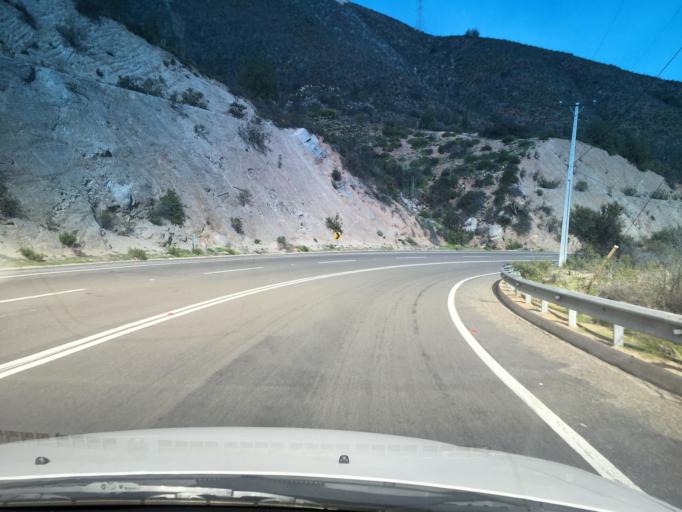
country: CL
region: Valparaiso
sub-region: Provincia de San Felipe
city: Llaillay
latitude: -33.0635
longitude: -71.0248
